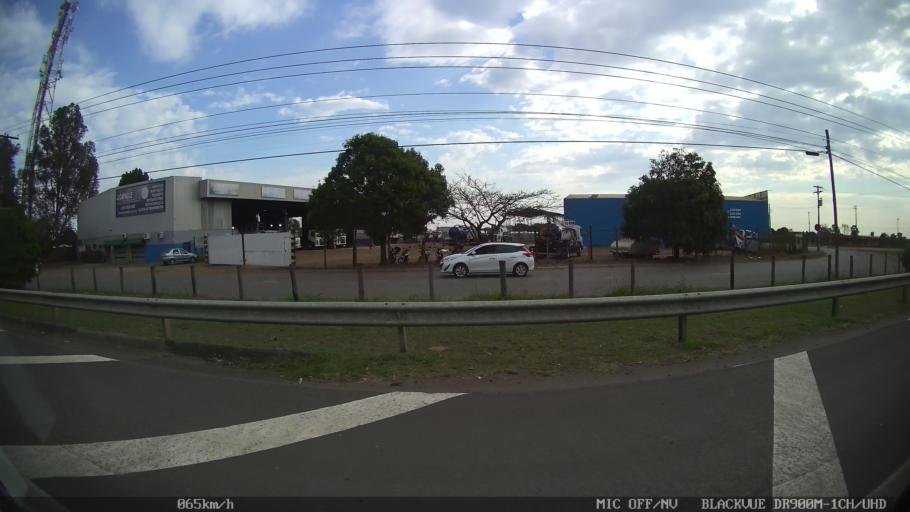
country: BR
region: Sao Paulo
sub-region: Paulinia
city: Paulinia
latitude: -22.7161
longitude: -47.1428
